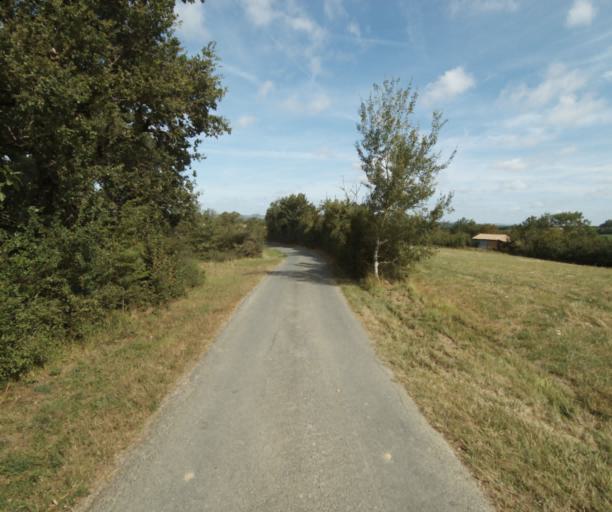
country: FR
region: Midi-Pyrenees
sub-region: Departement du Tarn
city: Soreze
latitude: 43.4771
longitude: 2.0965
